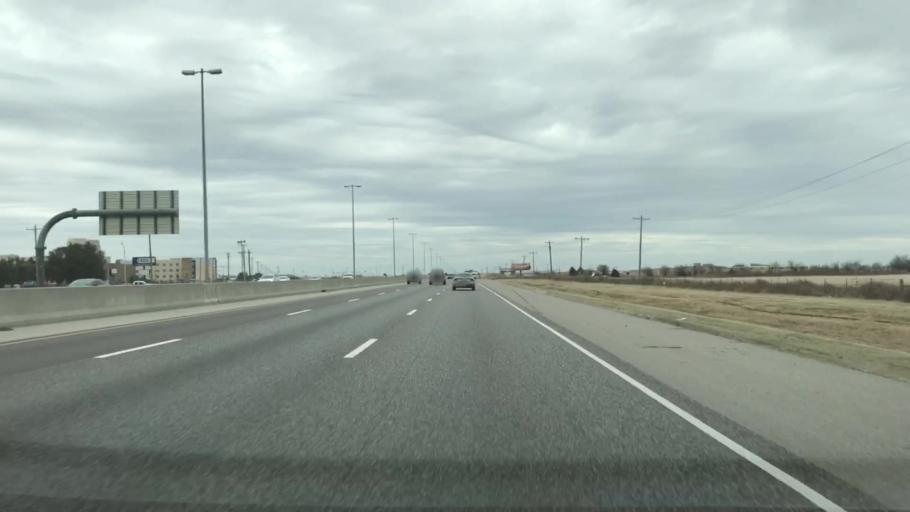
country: US
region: Oklahoma
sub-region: Cleveland County
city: Norman
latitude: 35.2525
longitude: -97.4854
